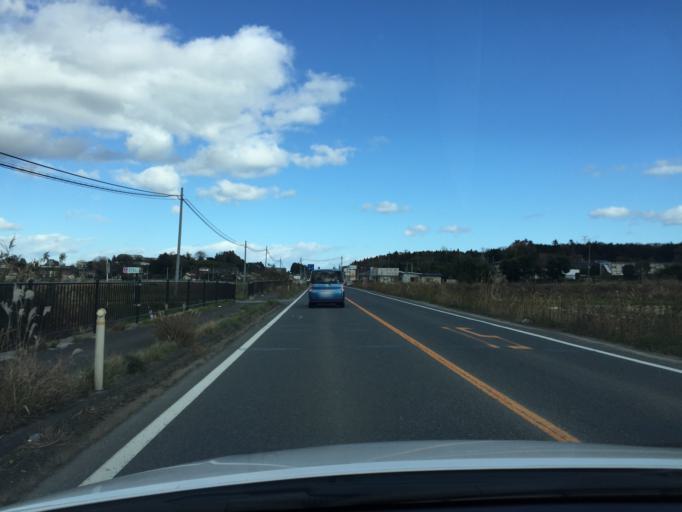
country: JP
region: Fukushima
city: Namie
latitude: 37.6013
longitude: 141.0047
